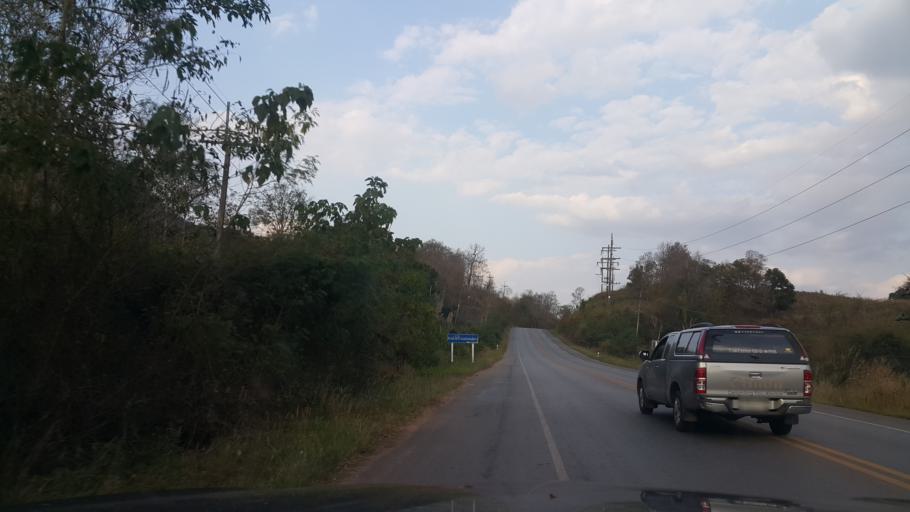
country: TH
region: Loei
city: Dan Sai
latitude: 17.3048
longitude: 101.2016
